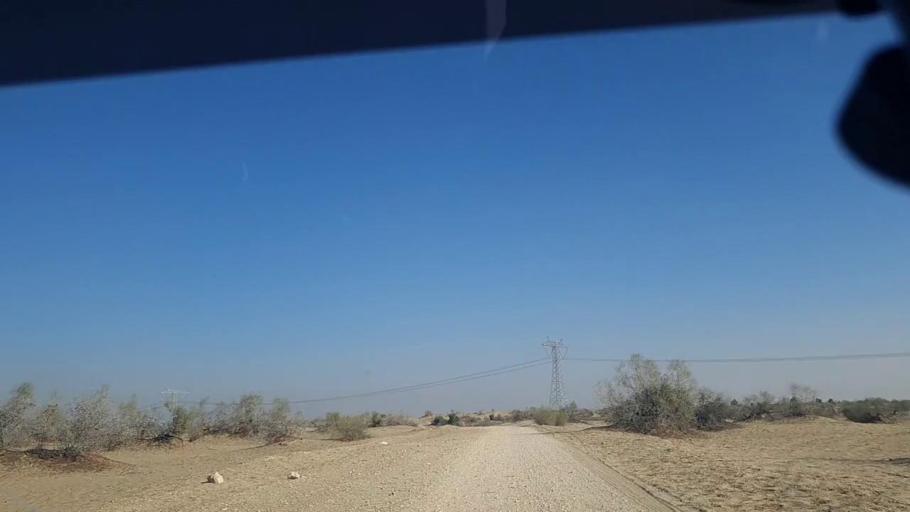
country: PK
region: Sindh
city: Khanpur
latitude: 27.6456
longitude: 69.4007
